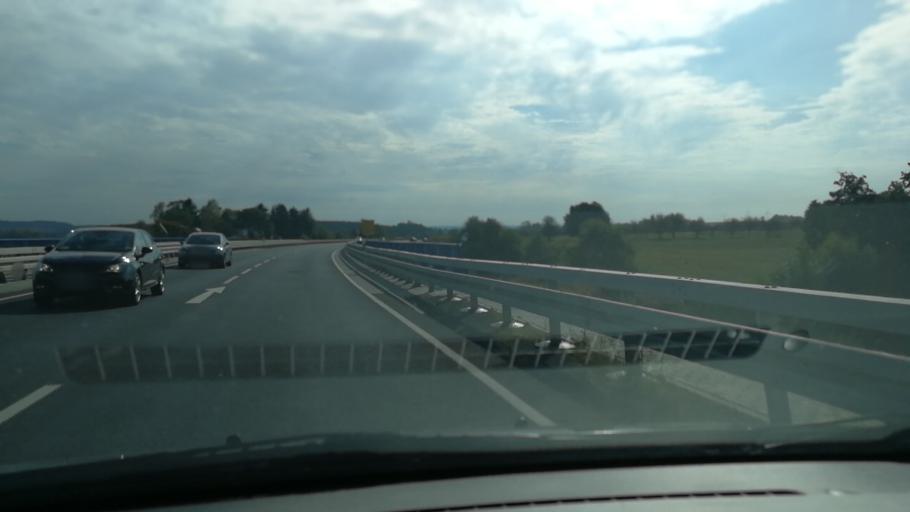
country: DE
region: Hesse
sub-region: Regierungsbezirk Darmstadt
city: Karben
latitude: 50.2738
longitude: 8.7603
